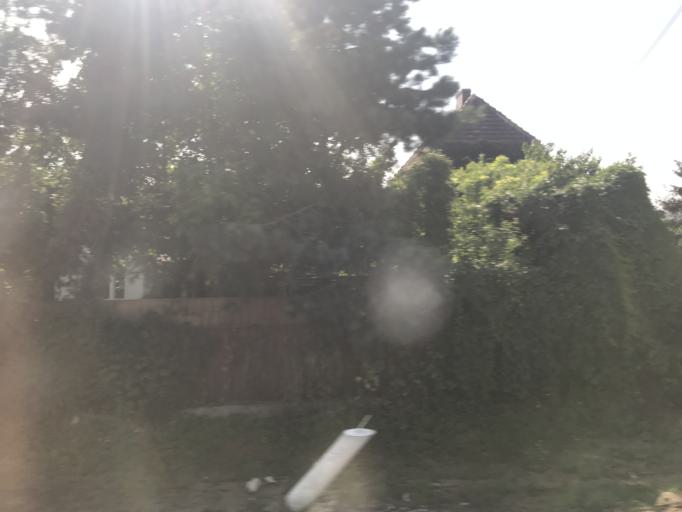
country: PL
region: Kujawsko-Pomorskie
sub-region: Powiat swiecki
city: Pruszcz
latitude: 53.3321
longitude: 18.1953
